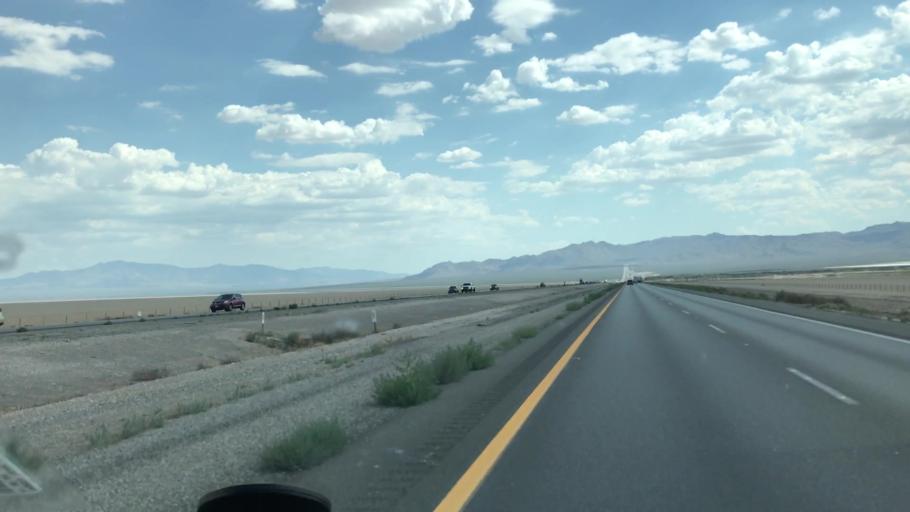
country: US
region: Nevada
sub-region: Clark County
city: Sandy Valley
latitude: 35.5871
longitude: -115.4001
